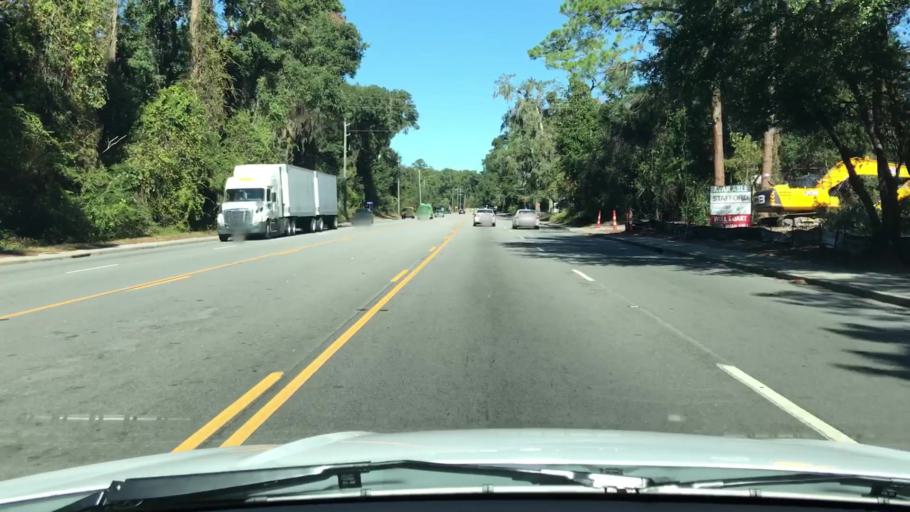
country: US
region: South Carolina
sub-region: Beaufort County
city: Burton
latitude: 32.4290
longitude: -80.7261
